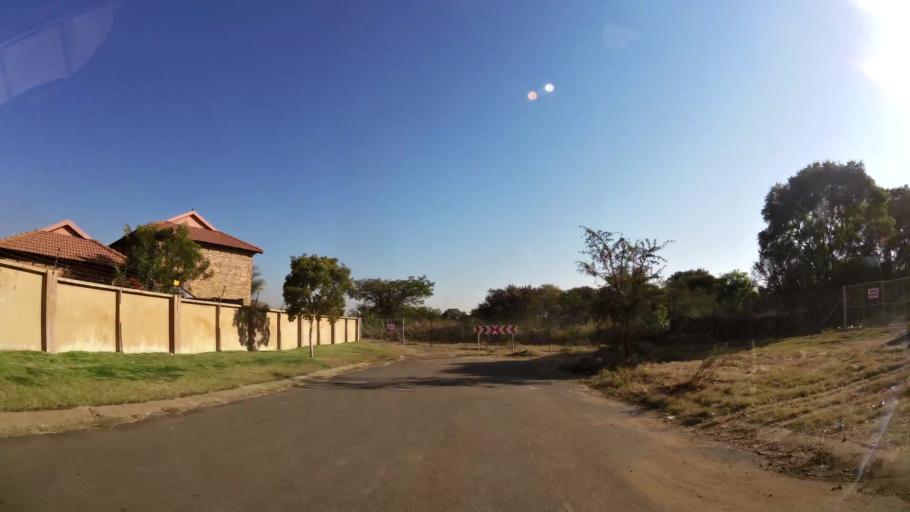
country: ZA
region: Gauteng
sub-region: City of Tshwane Metropolitan Municipality
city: Pretoria
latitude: -25.6703
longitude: 28.2119
